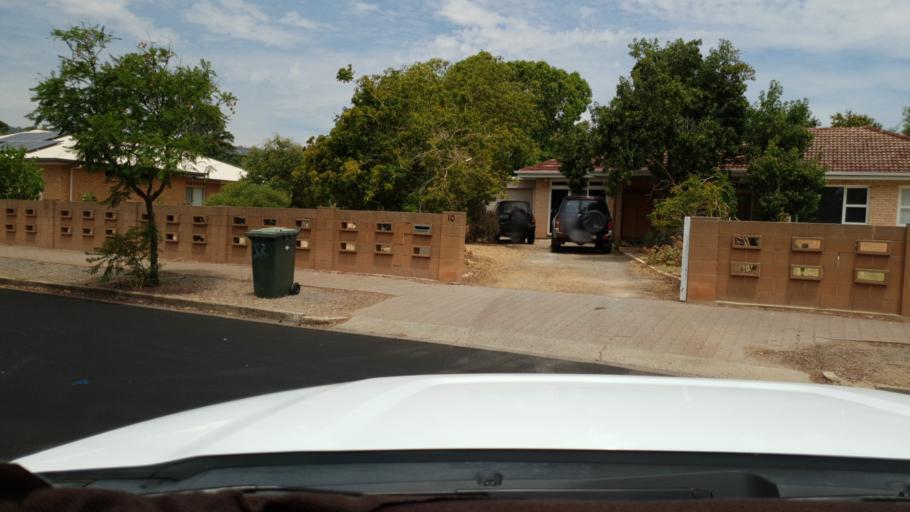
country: AU
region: South Australia
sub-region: Marion
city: Clovelly Park
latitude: -34.9995
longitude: 138.5815
